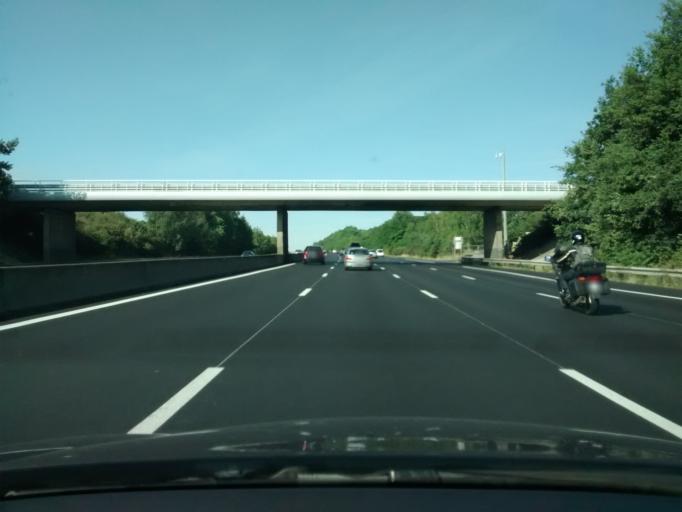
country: FR
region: Ile-de-France
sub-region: Departement de l'Essonne
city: Angervilliers
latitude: 48.5995
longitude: 2.0591
